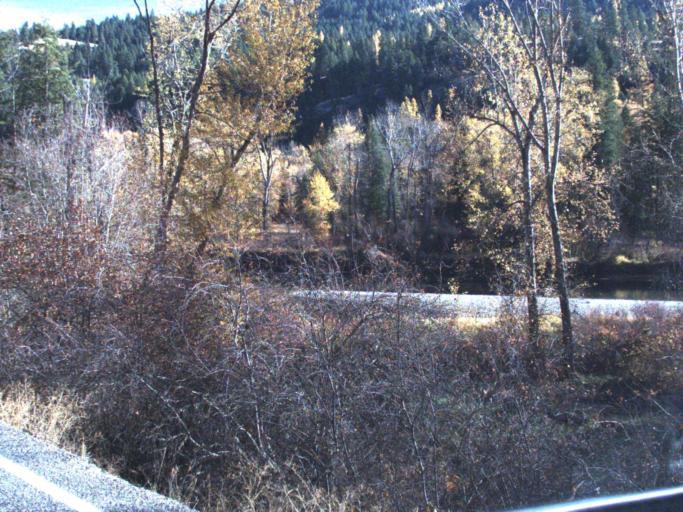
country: CA
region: British Columbia
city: Grand Forks
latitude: 48.9143
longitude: -118.5692
